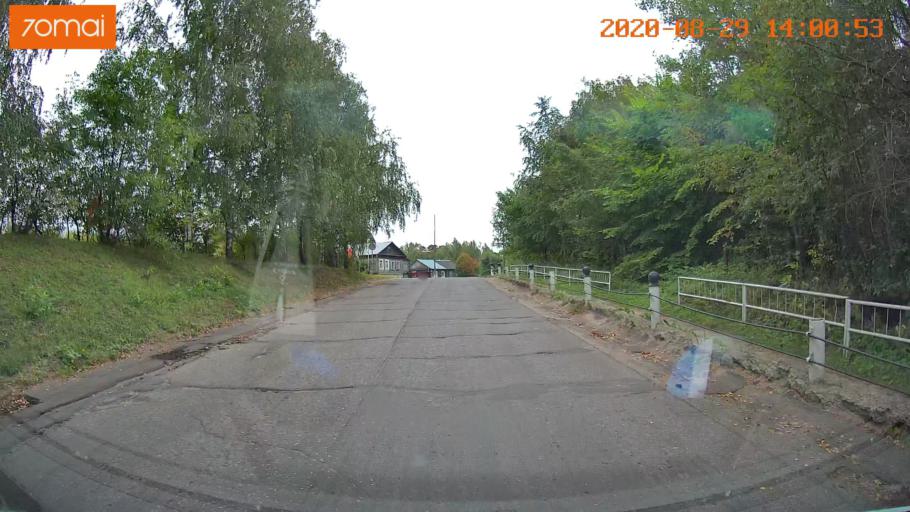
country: RU
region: Ivanovo
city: Yur'yevets
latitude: 57.3137
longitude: 43.1072
